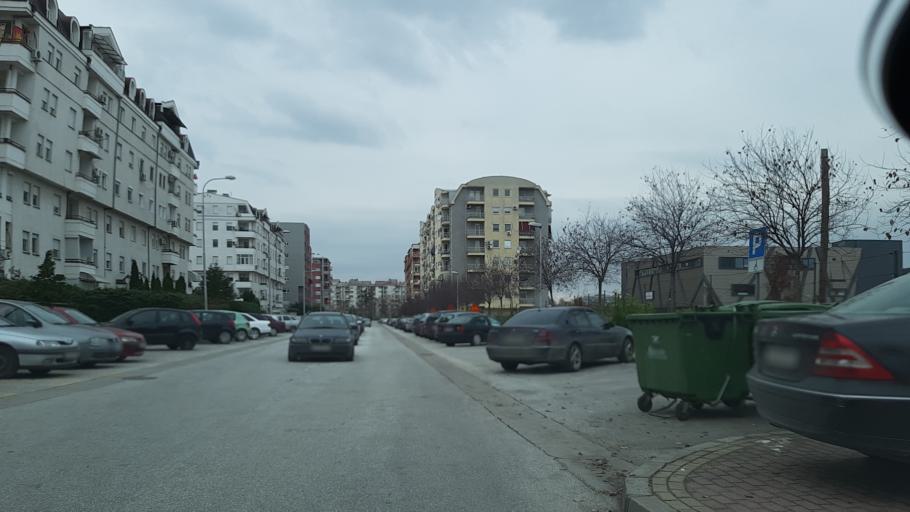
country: MK
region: Kisela Voda
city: Usje
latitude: 41.9799
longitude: 21.4736
